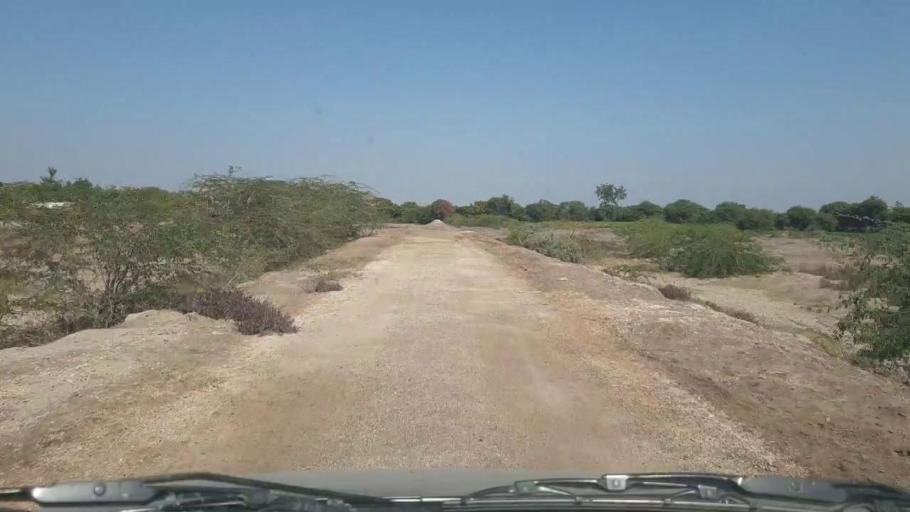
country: PK
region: Sindh
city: Samaro
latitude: 25.2433
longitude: 69.3261
